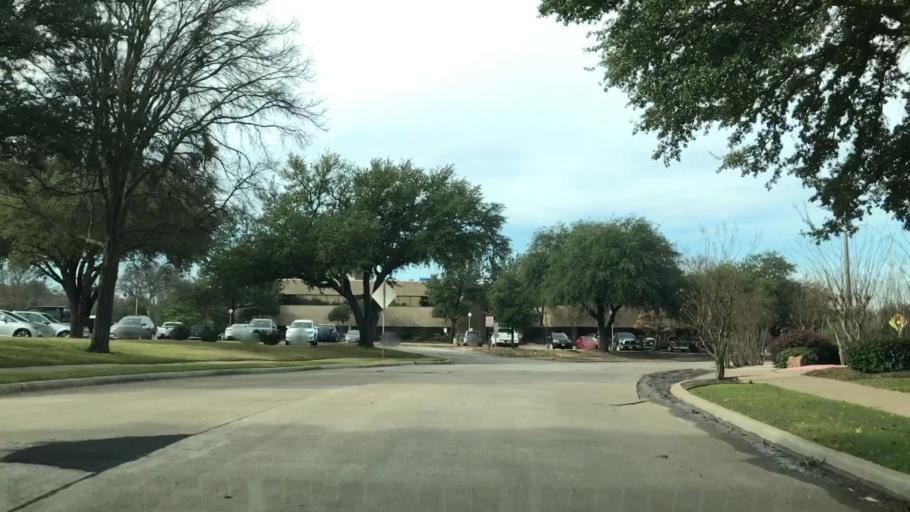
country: US
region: Texas
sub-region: Dallas County
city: Richardson
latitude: 32.9734
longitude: -96.7219
